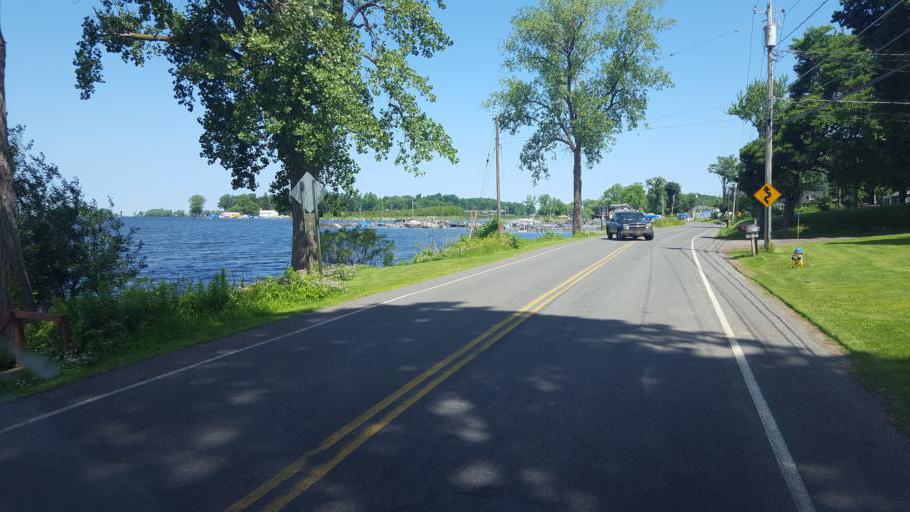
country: US
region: New York
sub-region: Wayne County
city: Sodus
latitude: 43.2560
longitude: -76.9372
